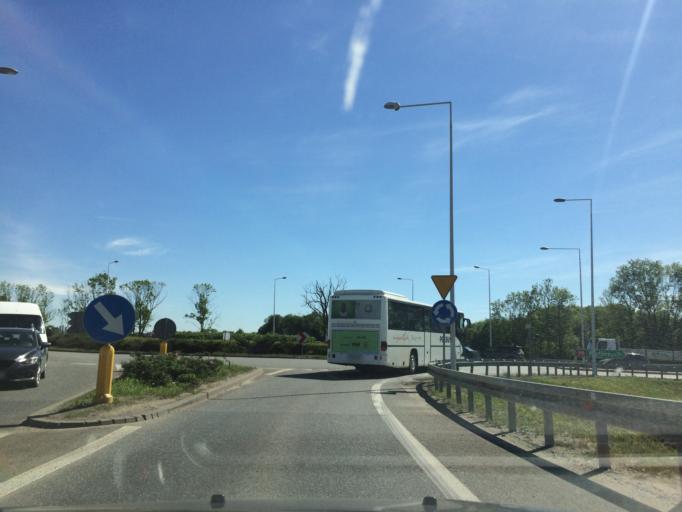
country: PL
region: Lower Silesian Voivodeship
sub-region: Powiat wroclawski
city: Tyniec Maly
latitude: 51.0317
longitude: 16.9328
